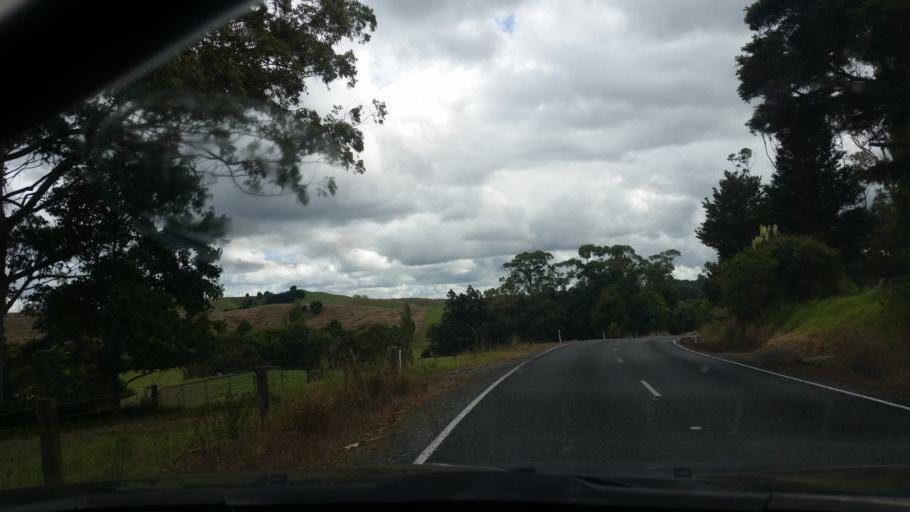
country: NZ
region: Northland
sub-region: Whangarei
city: Ruakaka
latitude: -35.9462
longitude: 174.2924
